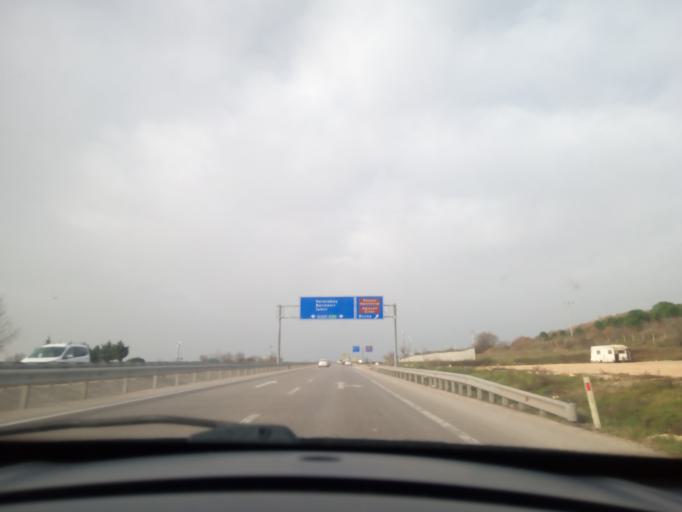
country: TR
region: Bursa
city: Mahmudiye
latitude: 40.2129
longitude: 28.6903
